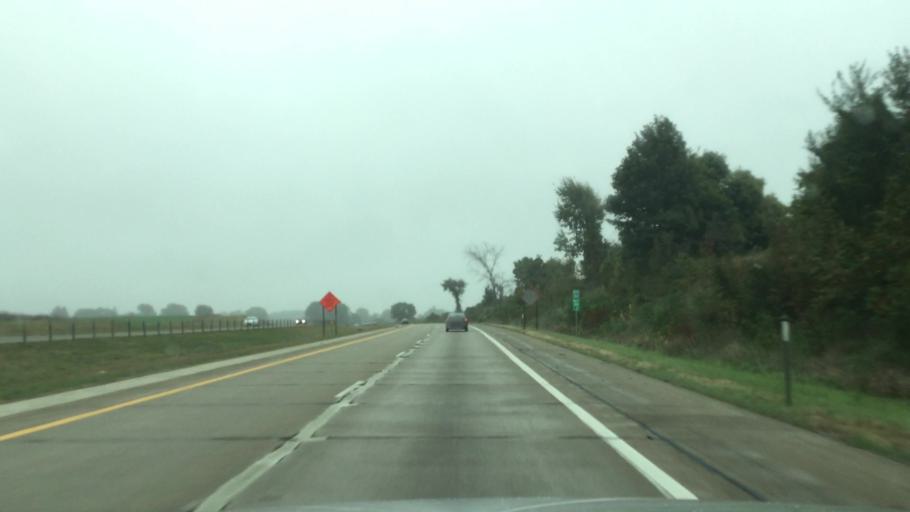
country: US
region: Michigan
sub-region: Van Buren County
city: Hartford
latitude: 42.1935
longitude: -86.1199
